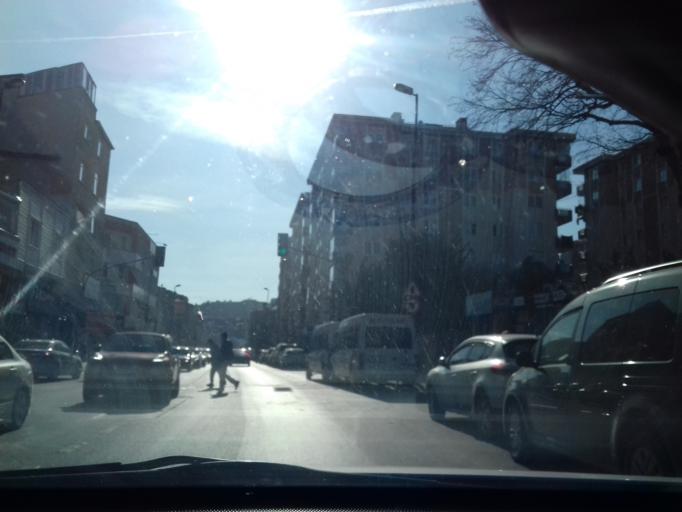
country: TR
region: Istanbul
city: Umraniye
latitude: 41.0186
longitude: 29.0800
